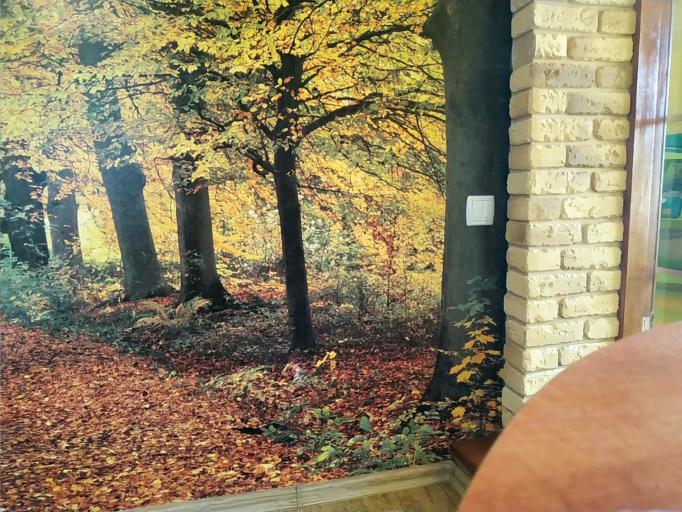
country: RU
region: Arkhangelskaya
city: Onega
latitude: 63.6704
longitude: 38.0965
